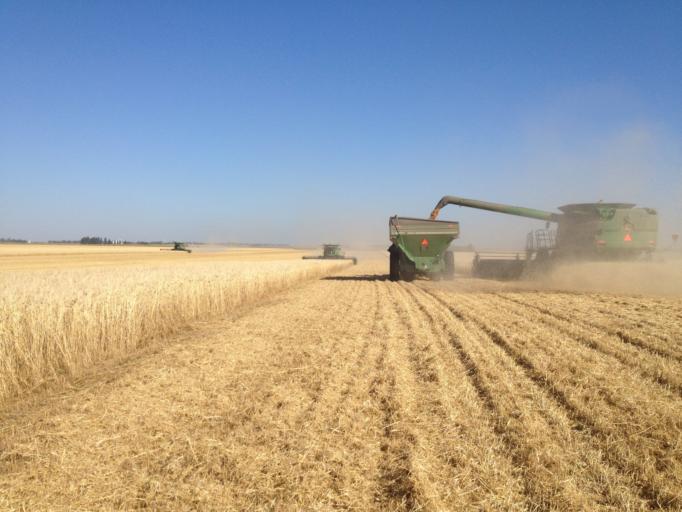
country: US
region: North Dakota
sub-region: McLean County
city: Garrison
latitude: 47.7178
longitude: -101.7892
